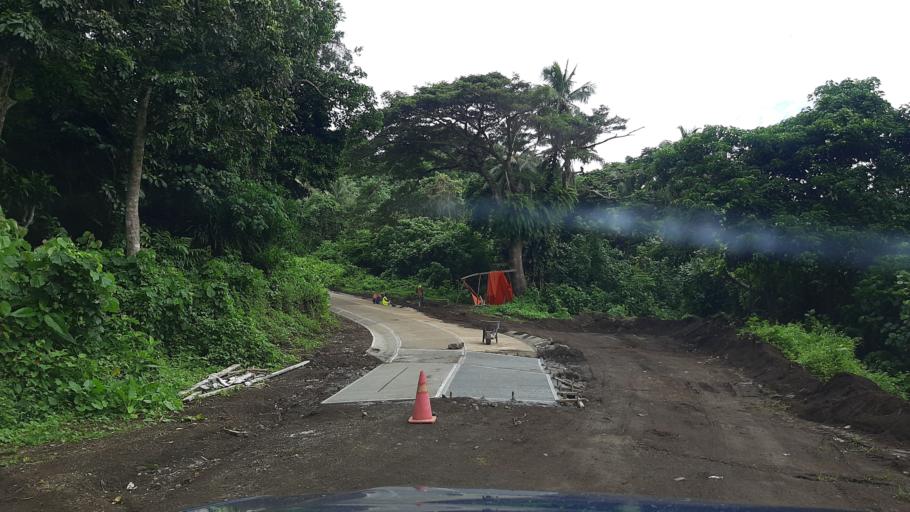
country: VU
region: Shefa
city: Port-Vila
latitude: -16.9012
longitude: 168.5727
